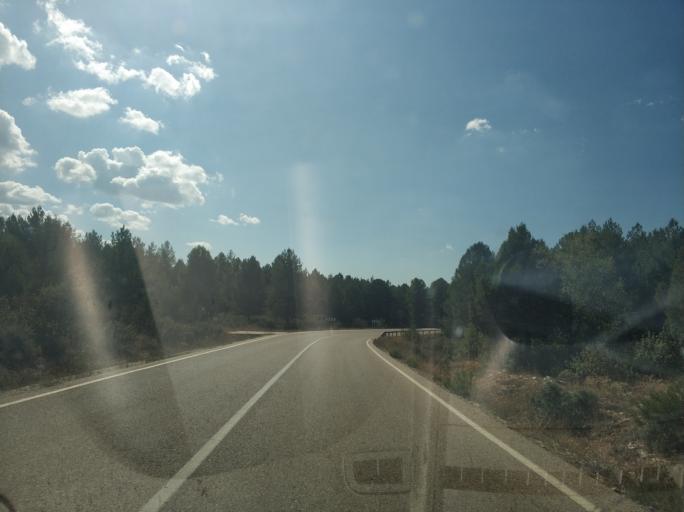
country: ES
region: Castille and Leon
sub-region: Provincia de Soria
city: Herrera de Soria
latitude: 41.7668
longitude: -3.0310
